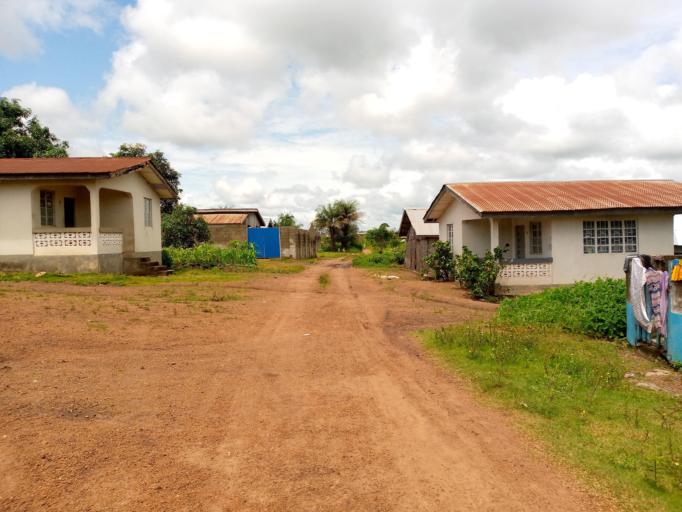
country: SL
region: Northern Province
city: Magburaka
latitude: 8.7213
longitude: -11.9243
